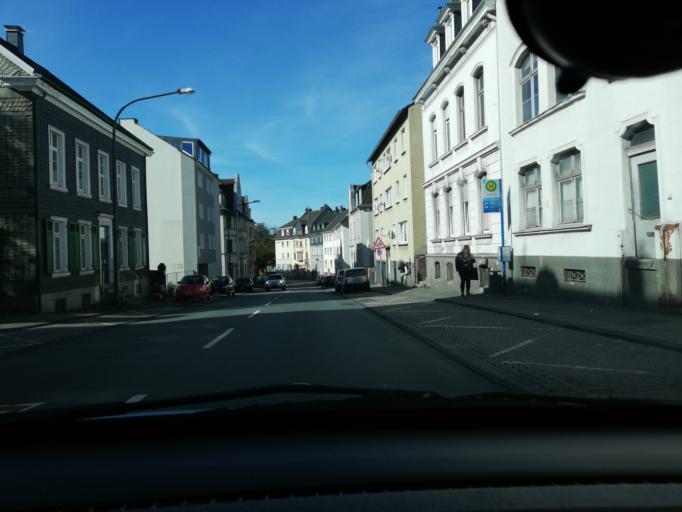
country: DE
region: North Rhine-Westphalia
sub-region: Regierungsbezirk Dusseldorf
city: Wuppertal
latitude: 51.2853
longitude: 7.2218
